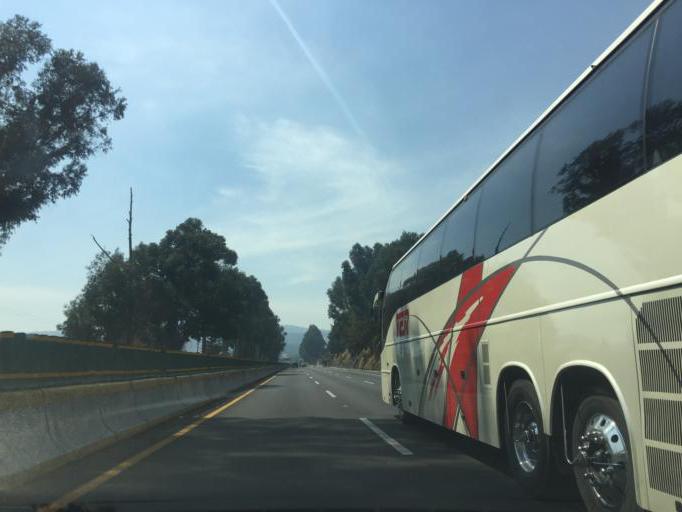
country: MX
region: Mexico City
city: Xochimilco
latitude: 19.1989
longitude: -99.1463
